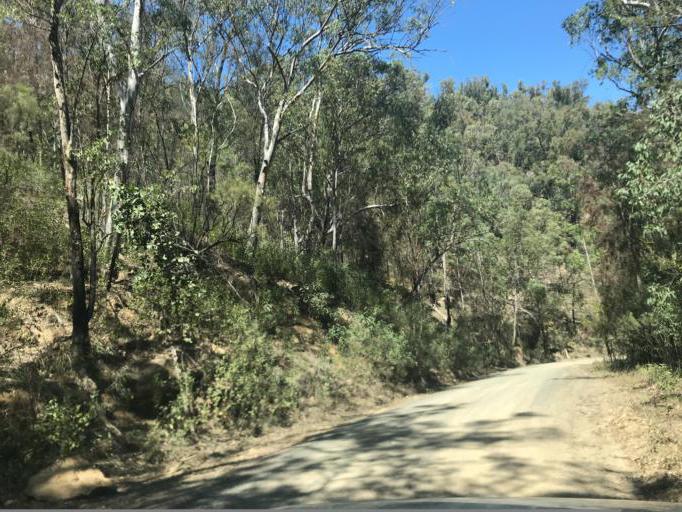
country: AU
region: New South Wales
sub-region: Wyong Shire
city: Little Jilliby
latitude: -33.1594
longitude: 151.0748
